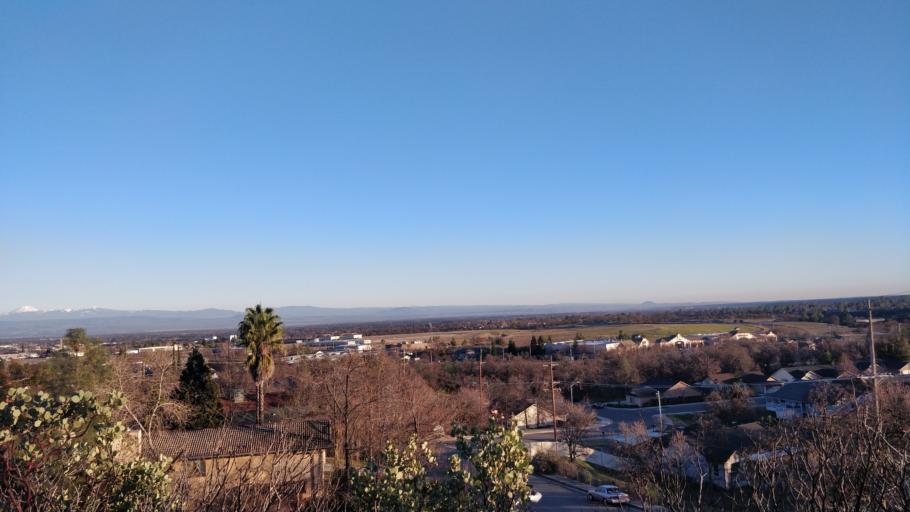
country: US
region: California
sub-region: Shasta County
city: Redding
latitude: 40.5782
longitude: -122.4195
